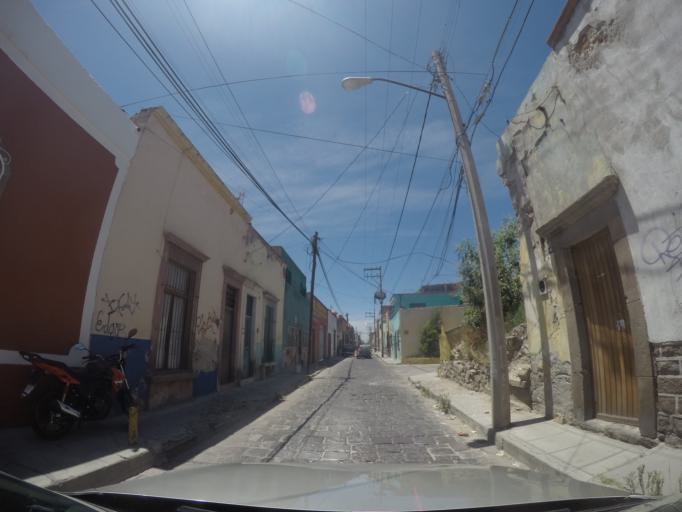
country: MX
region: San Luis Potosi
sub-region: San Luis Potosi
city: San Luis Potosi
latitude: 22.1561
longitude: -100.9816
